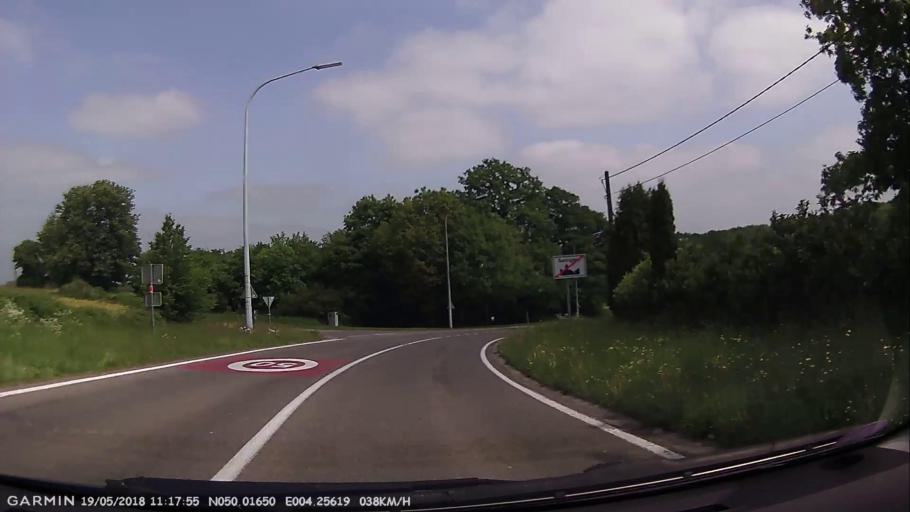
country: BE
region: Wallonia
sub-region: Province du Hainaut
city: Chimay
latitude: 50.0166
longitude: 4.2562
